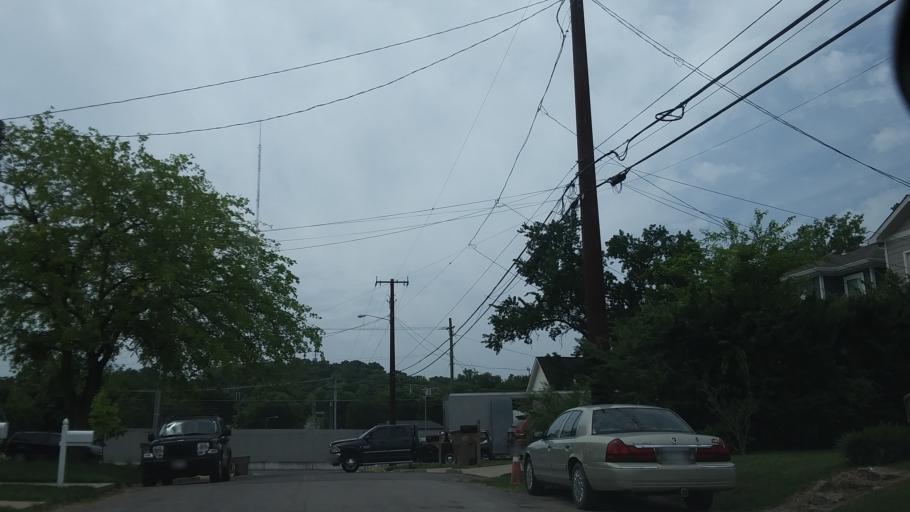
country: US
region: Tennessee
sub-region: Davidson County
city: Belle Meade
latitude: 36.1515
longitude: -86.8678
